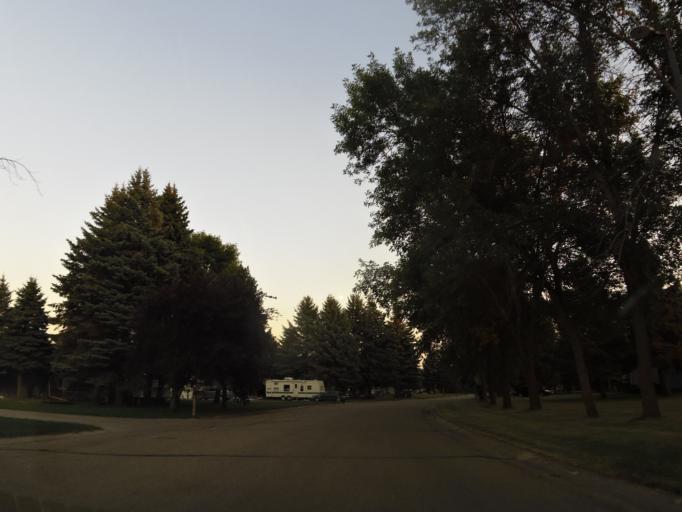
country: US
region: North Dakota
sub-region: Grand Forks County
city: Grand Forks
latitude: 47.8563
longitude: -97.0093
